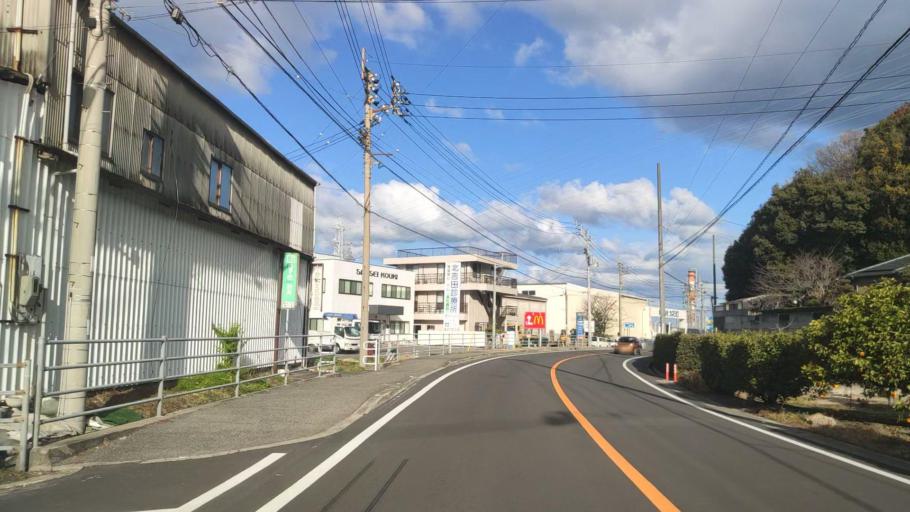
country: JP
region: Ehime
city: Masaki-cho
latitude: 33.8417
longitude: 132.7081
